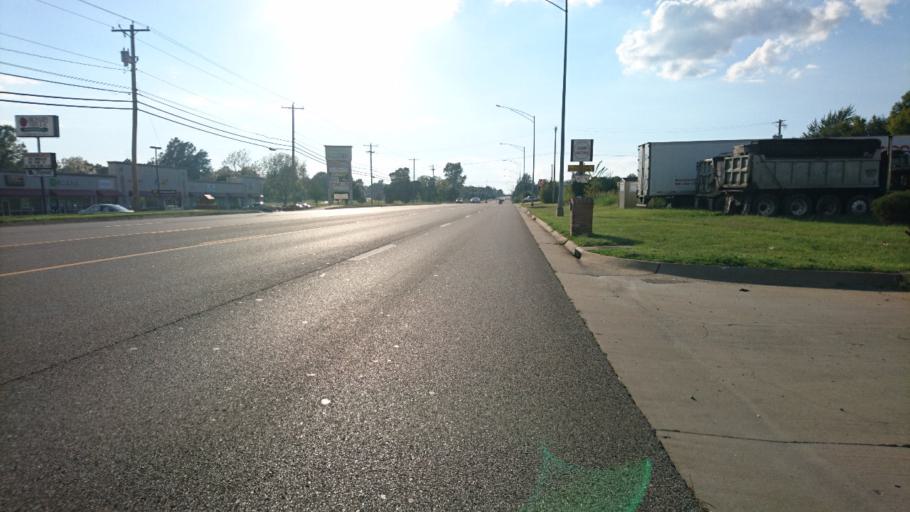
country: US
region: Missouri
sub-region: Greene County
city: Springfield
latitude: 37.2124
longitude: -93.3560
